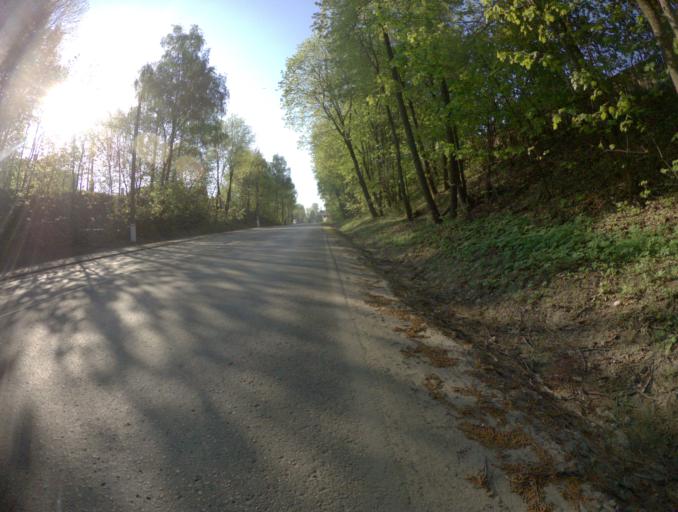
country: RU
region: Vladimir
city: Vyazniki
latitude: 56.2403
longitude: 42.1704
